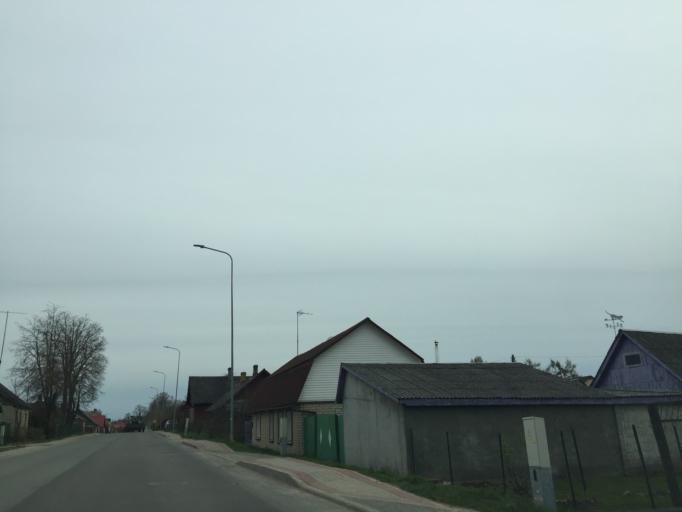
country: LV
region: Ludzas Rajons
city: Ludza
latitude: 56.5585
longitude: 27.7242
